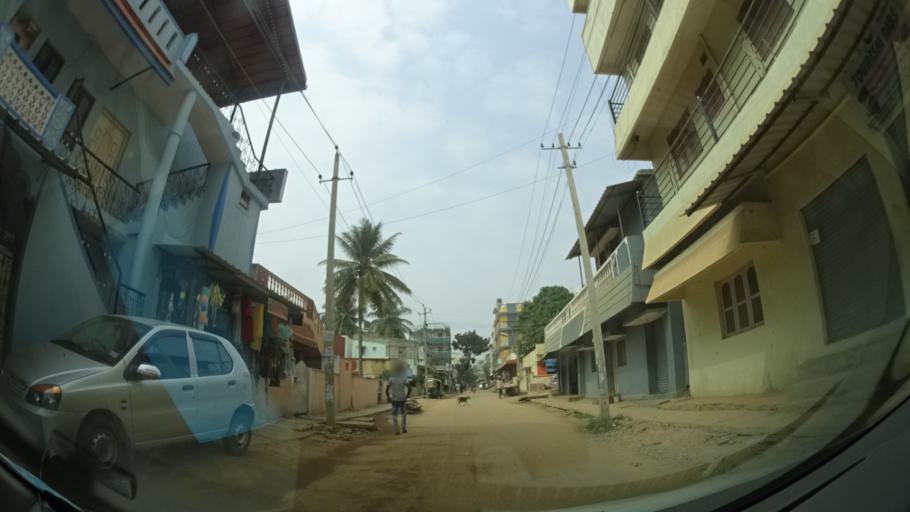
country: IN
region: Karnataka
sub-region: Bangalore Rural
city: Hoskote
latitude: 12.9726
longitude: 77.7553
